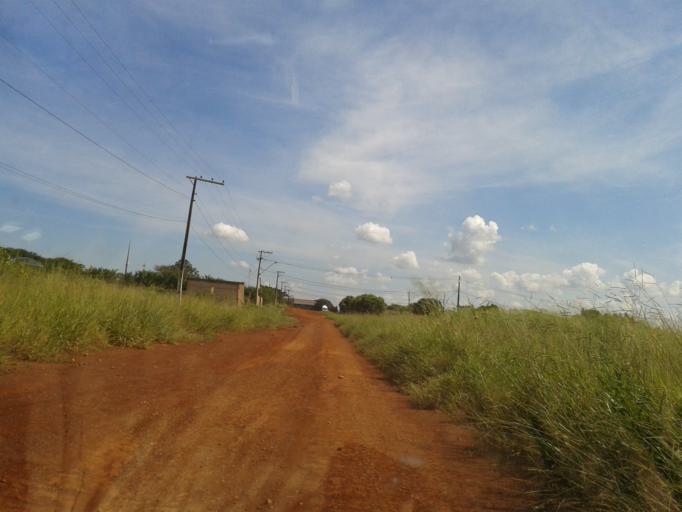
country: BR
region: Goias
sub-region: Itumbiara
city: Itumbiara
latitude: -18.4262
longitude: -49.1877
